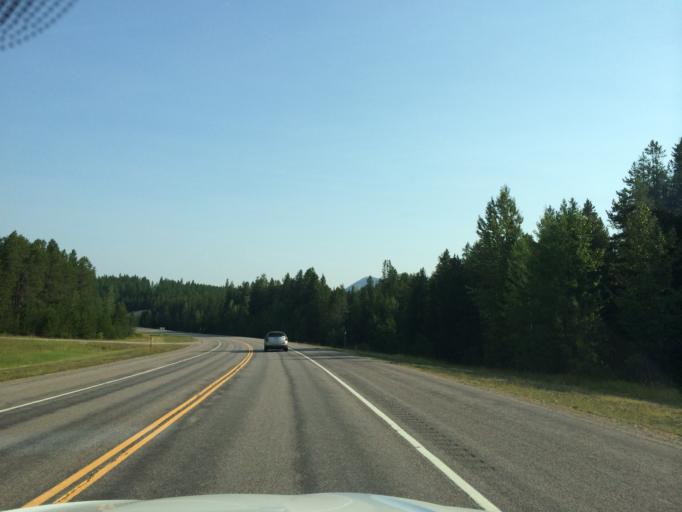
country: US
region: Montana
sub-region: Flathead County
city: Columbia Falls
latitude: 48.4672
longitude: -113.9968
